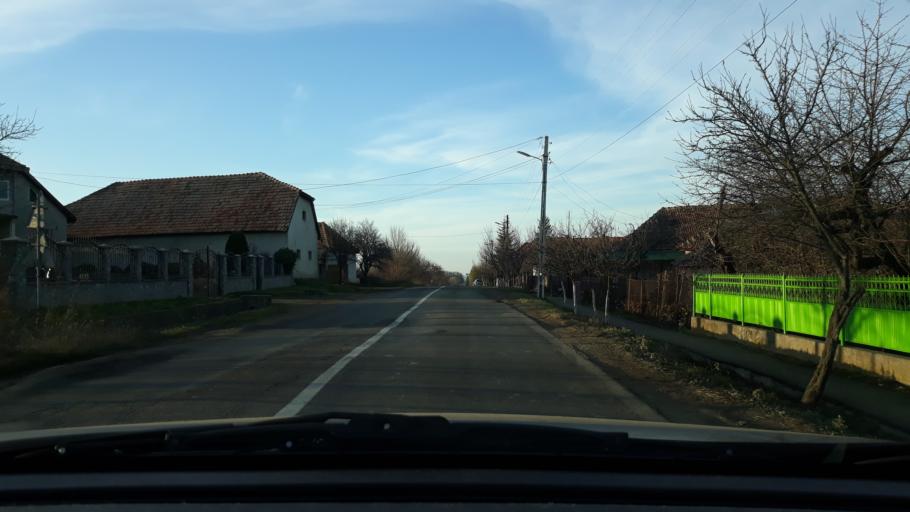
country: RO
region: Bihor
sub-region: Comuna Balc
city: Balc
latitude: 47.2731
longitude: 22.4896
